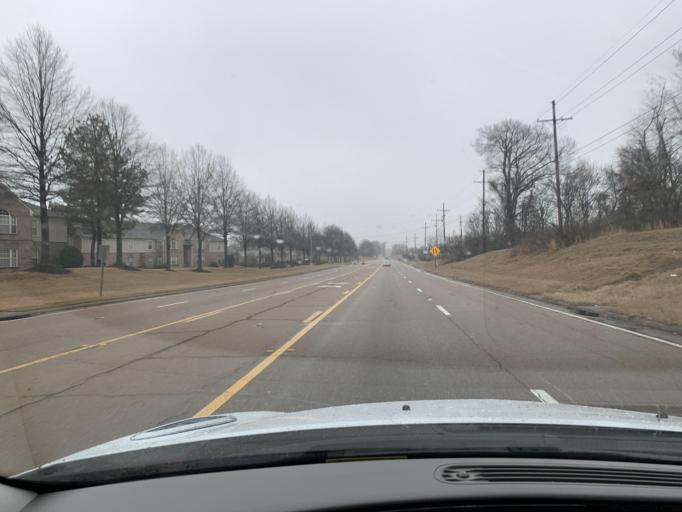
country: US
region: Mississippi
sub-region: De Soto County
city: Horn Lake
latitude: 34.9311
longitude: -90.0124
